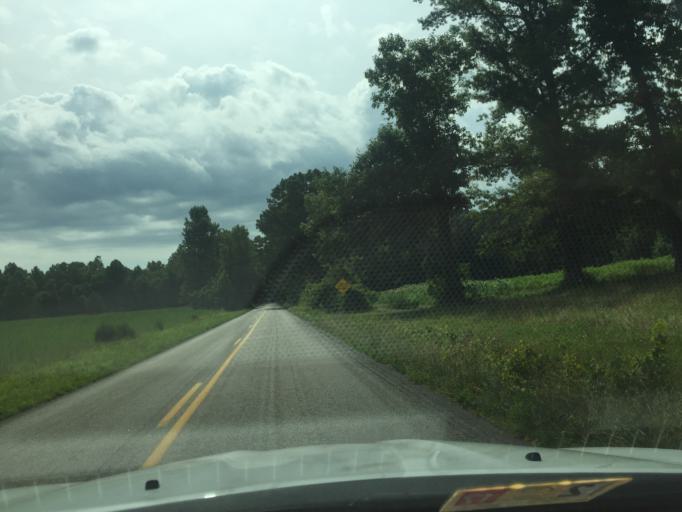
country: US
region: Virginia
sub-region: Charles City County
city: Charles City
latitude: 37.4117
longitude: -77.0382
